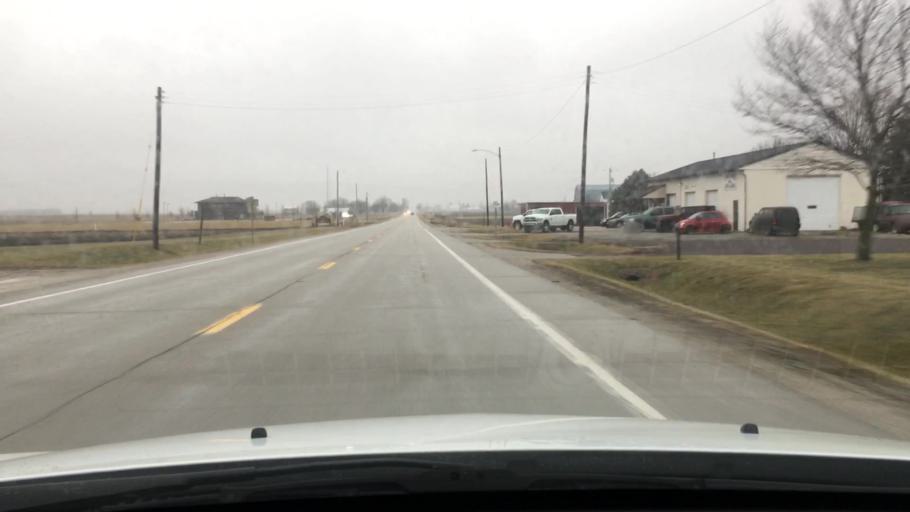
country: US
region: Illinois
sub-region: Livingston County
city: Flanagan
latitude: 40.8710
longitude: -88.8614
